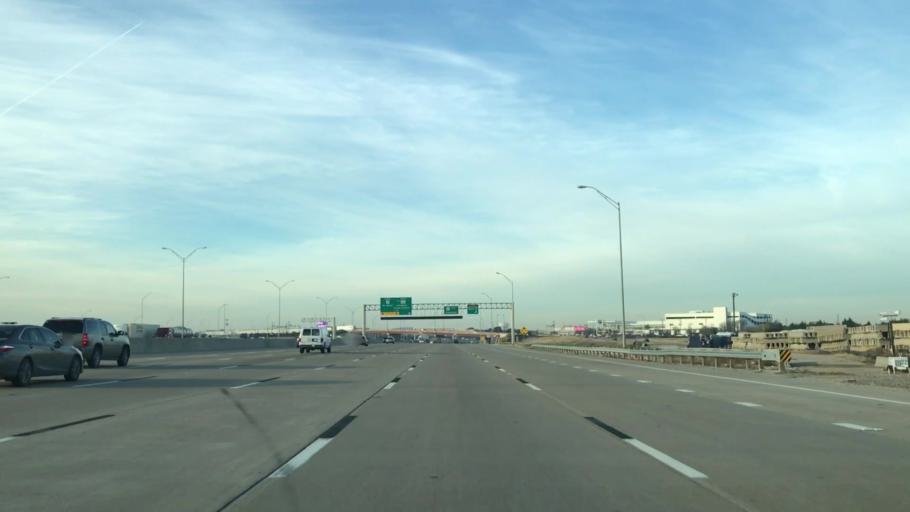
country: US
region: Texas
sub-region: Tarrant County
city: Grapevine
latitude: 32.9265
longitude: -97.0554
